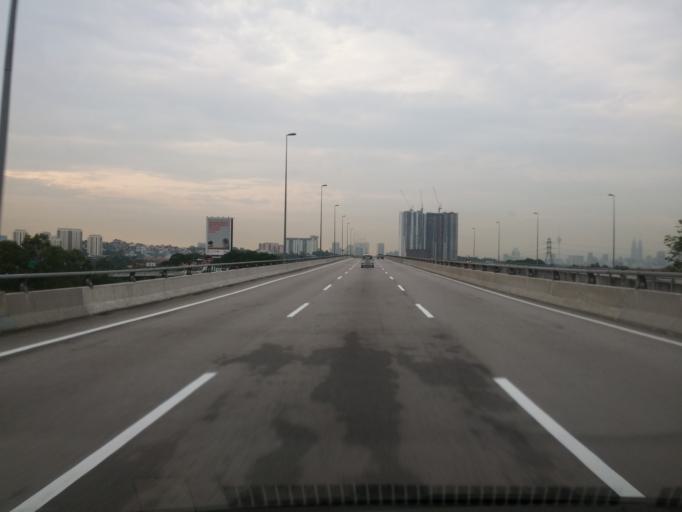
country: MY
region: Kuala Lumpur
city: Kuala Lumpur
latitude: 3.0926
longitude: 101.6961
